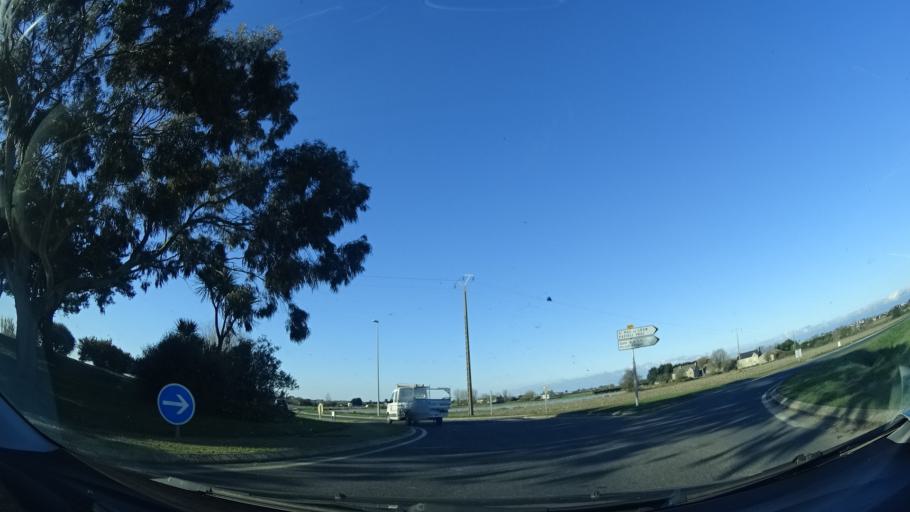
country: FR
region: Brittany
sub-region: Departement du Finistere
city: Saint-Pol-de-Leon
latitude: 48.6637
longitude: -3.9885
